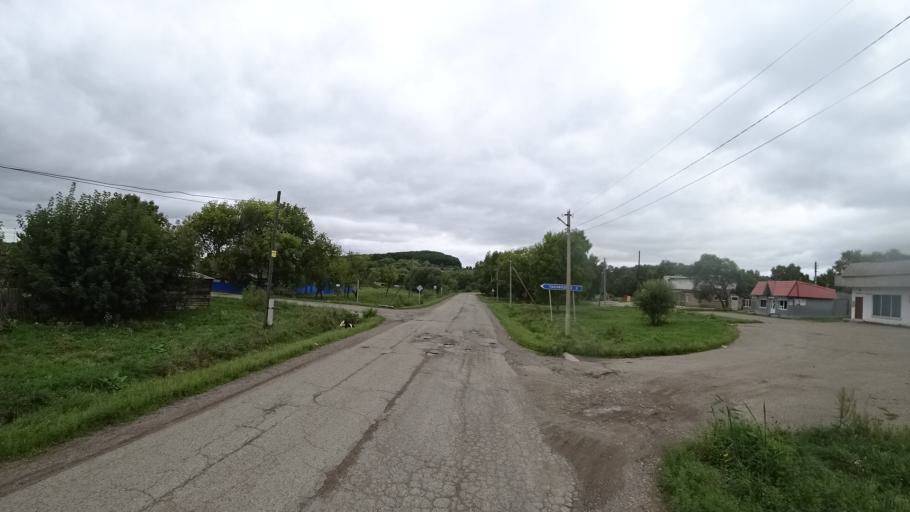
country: RU
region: Primorskiy
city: Chernigovka
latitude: 44.4571
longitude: 132.5929
